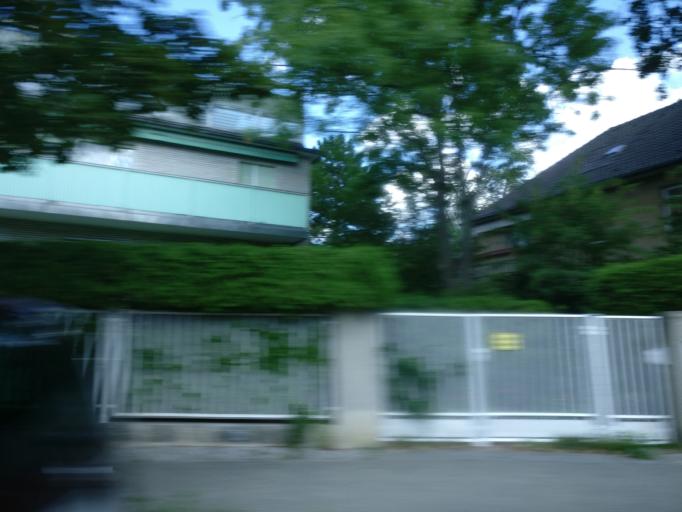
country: DE
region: Berlin
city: Halensee
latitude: 52.4915
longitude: 13.3068
